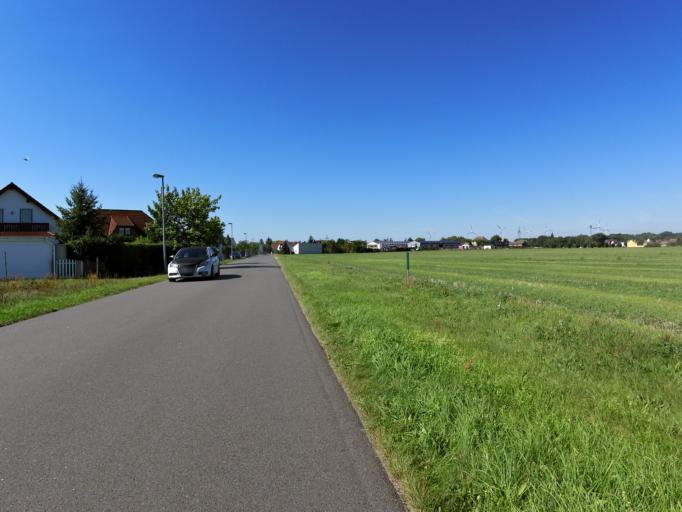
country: DE
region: Saxony-Anhalt
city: Muhlanger
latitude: 51.8439
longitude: 12.7482
